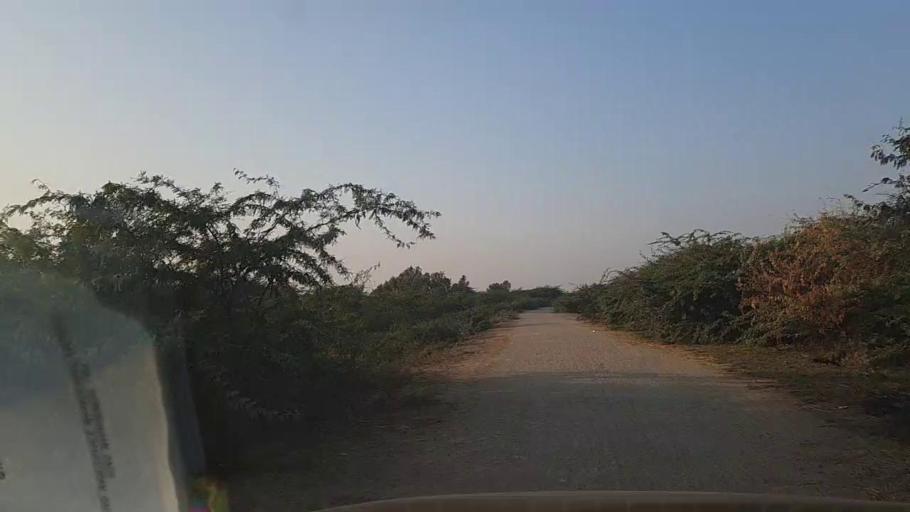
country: PK
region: Sindh
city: Keti Bandar
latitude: 24.3092
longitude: 67.6018
